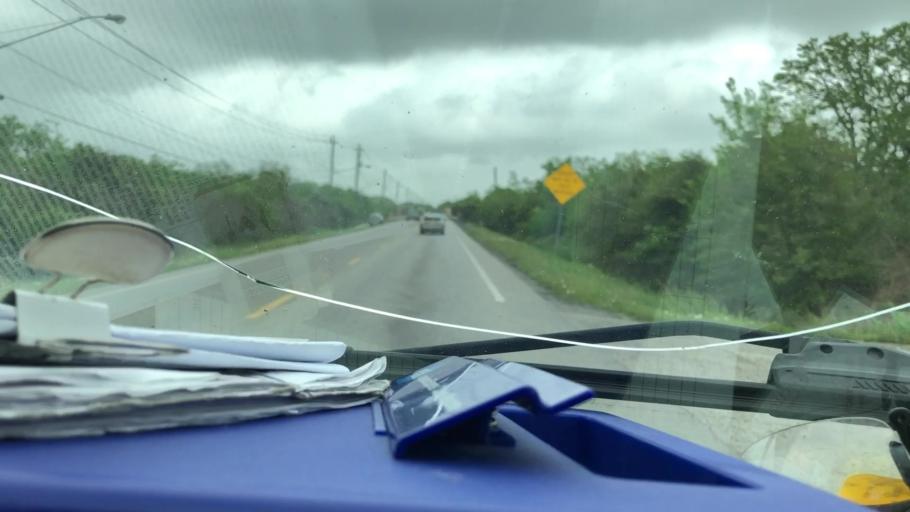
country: US
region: Texas
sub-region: Galveston County
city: Bacliff
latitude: 29.4841
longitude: -94.9690
